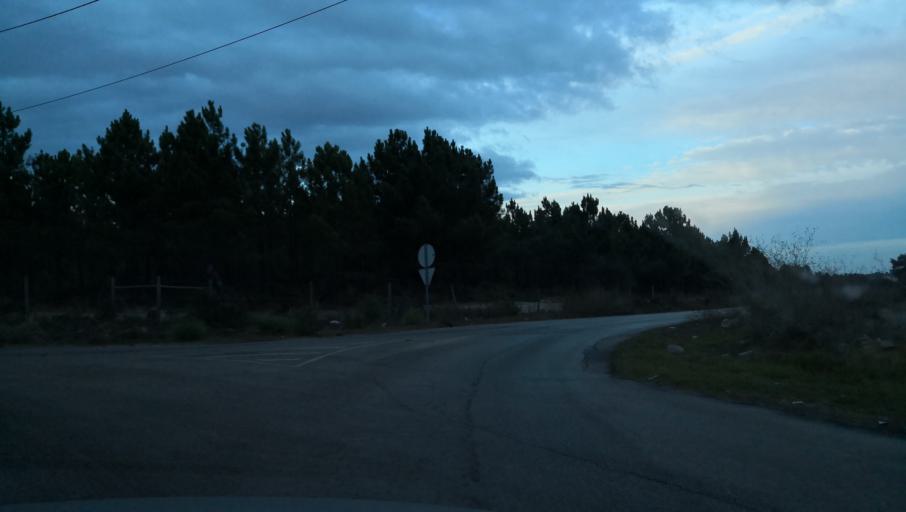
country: PT
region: Setubal
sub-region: Almada
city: Charneca
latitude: 38.5947
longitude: -9.1592
